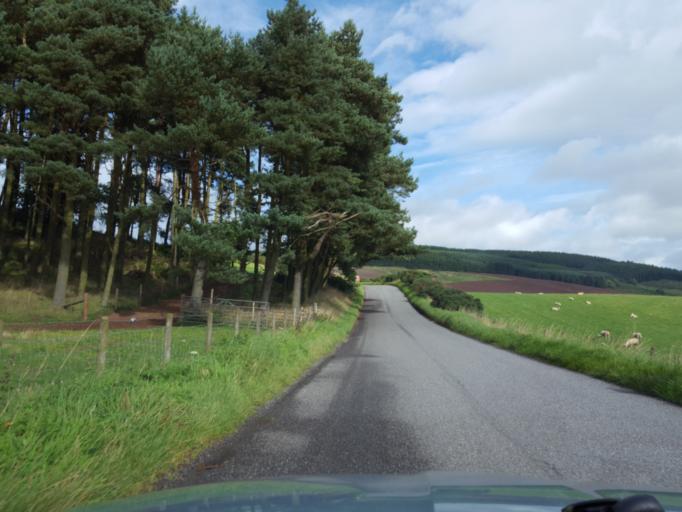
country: GB
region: Scotland
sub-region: Aberdeenshire
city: Laurencekirk
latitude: 56.8732
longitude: -2.5502
